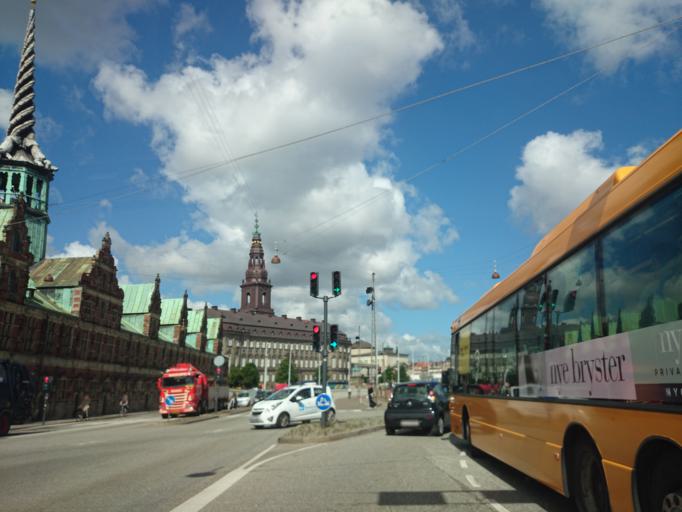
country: DK
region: Capital Region
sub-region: Kobenhavn
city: Christianshavn
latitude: 55.6756
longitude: 12.5851
